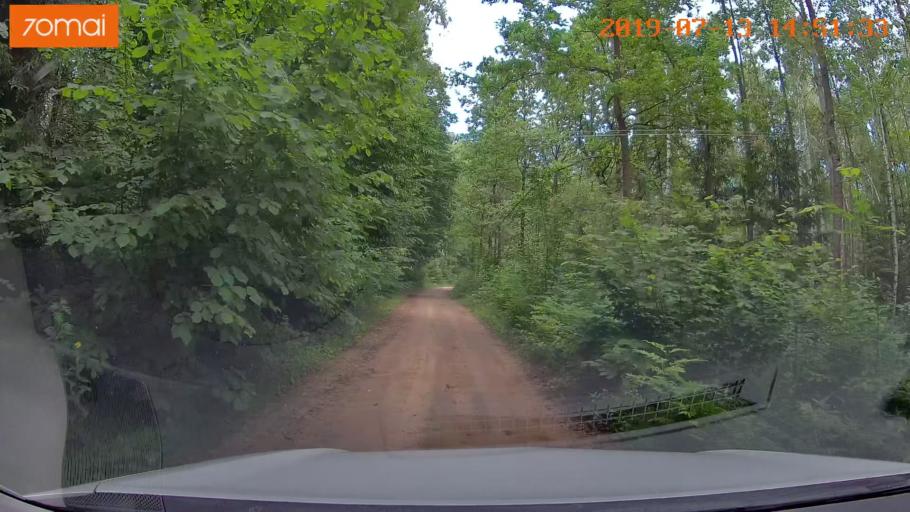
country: BY
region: Mogilev
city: Asipovichy
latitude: 53.2110
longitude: 28.7504
